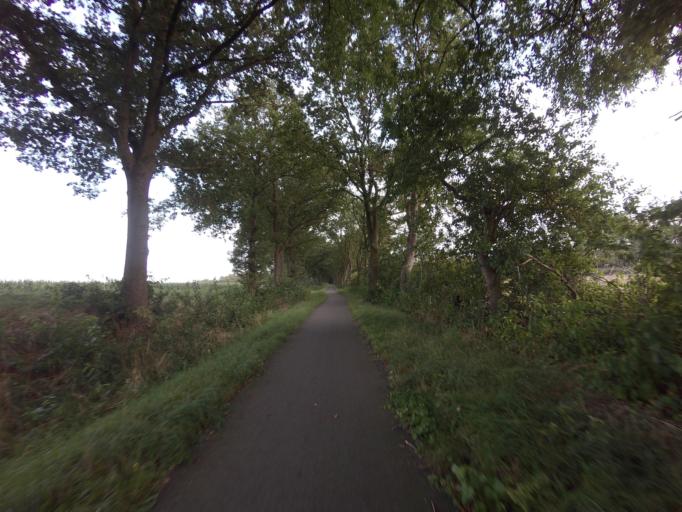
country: DE
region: Lower Saxony
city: Wielen
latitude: 52.5451
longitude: 6.6945
